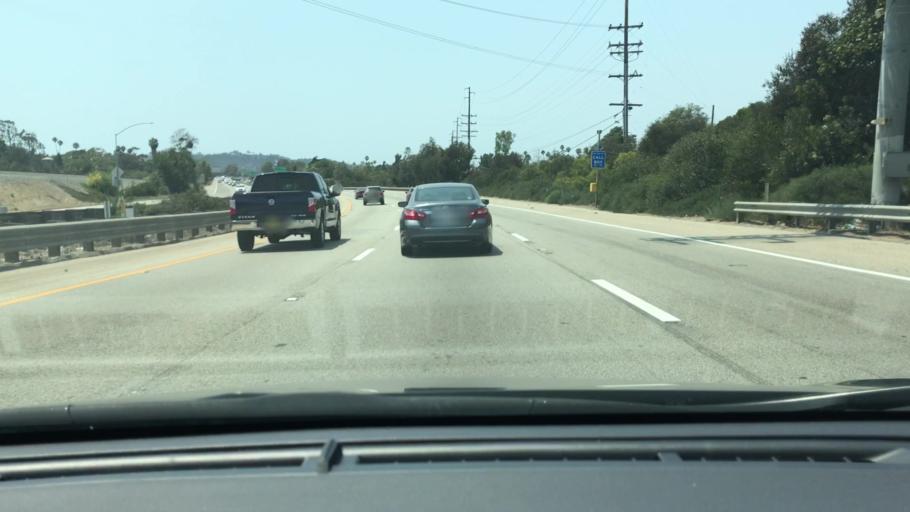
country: US
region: California
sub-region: Santa Barbara County
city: Montecito
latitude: 34.4232
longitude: -119.6588
